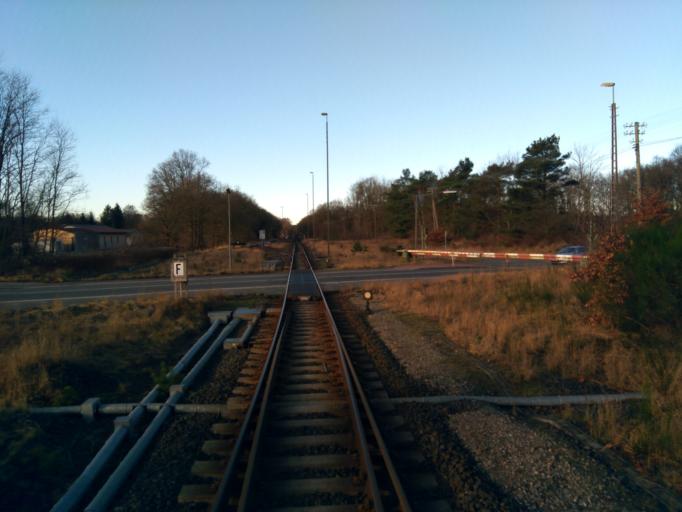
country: DE
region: Lower Saxony
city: Munster
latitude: 52.9945
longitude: 10.0905
